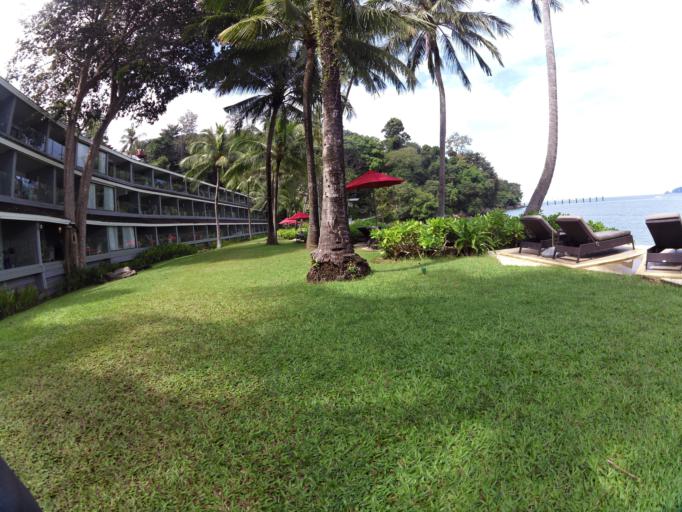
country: TH
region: Phuket
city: Patong
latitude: 7.8868
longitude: 98.2838
